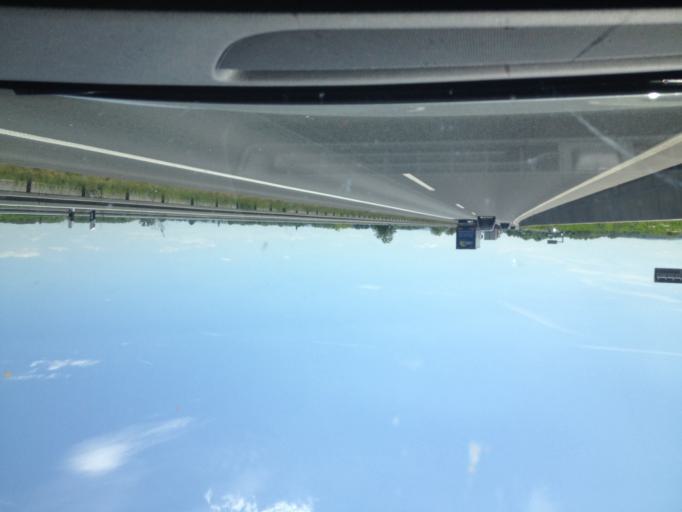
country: DE
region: North Rhine-Westphalia
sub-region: Regierungsbezirk Koln
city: Euskirchen
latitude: 50.6761
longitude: 6.7393
